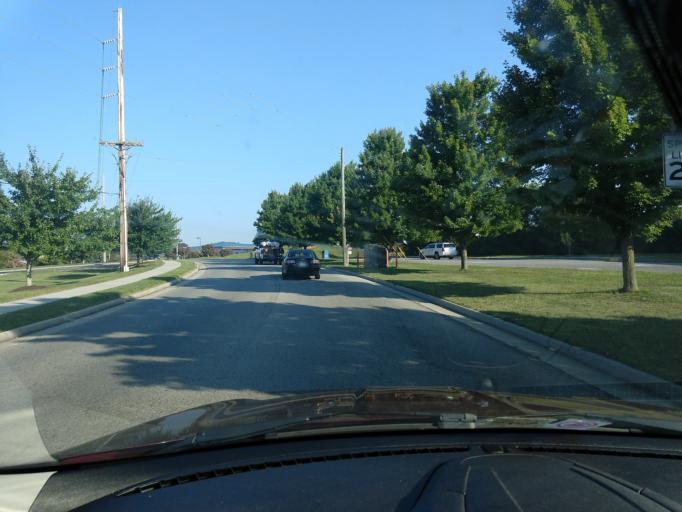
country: US
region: Virginia
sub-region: Montgomery County
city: Merrimac
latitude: 37.1679
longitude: -80.4176
